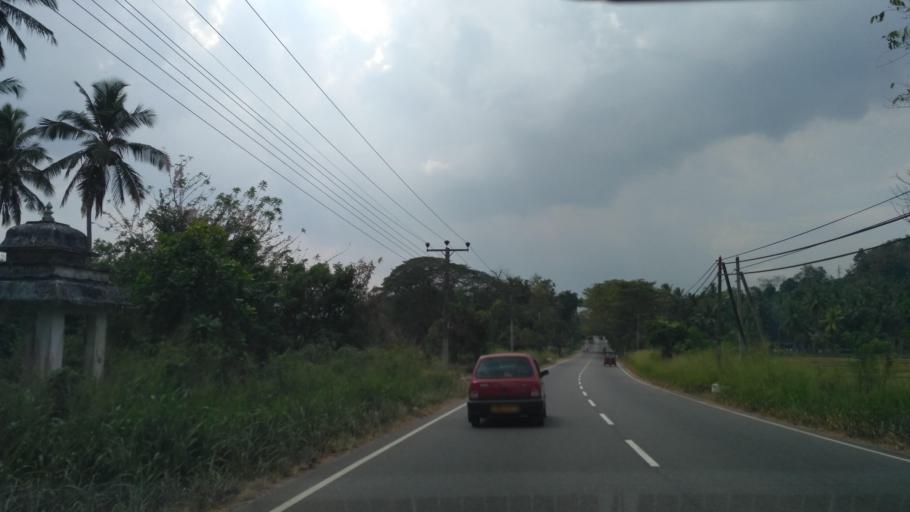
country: LK
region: North Western
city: Kuliyapitiya
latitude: 7.3254
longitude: 80.1100
